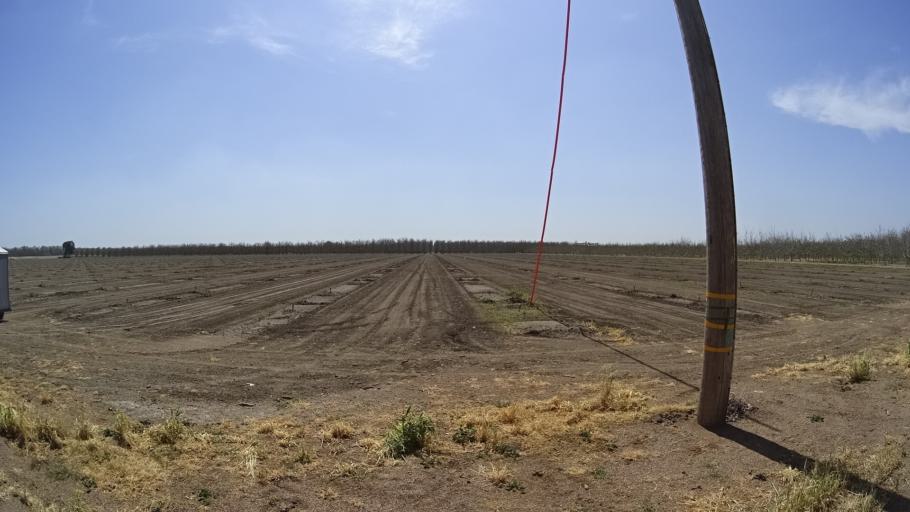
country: US
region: California
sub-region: Glenn County
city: Willows
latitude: 39.5108
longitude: -122.0129
